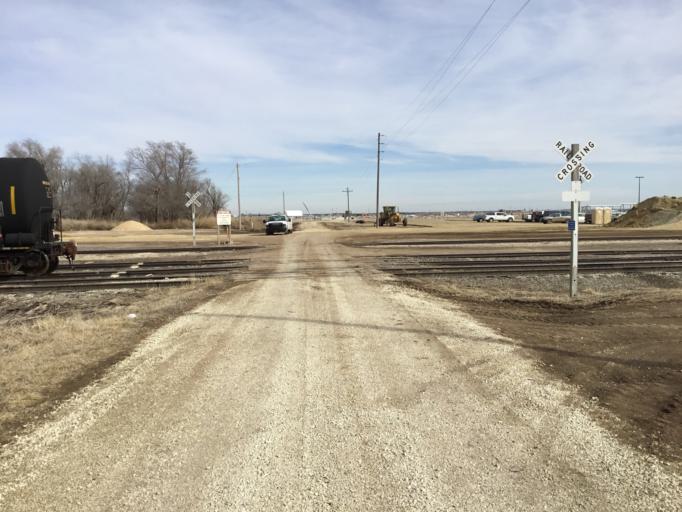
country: US
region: Kansas
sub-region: McPherson County
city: McPherson
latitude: 38.3706
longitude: -97.7874
